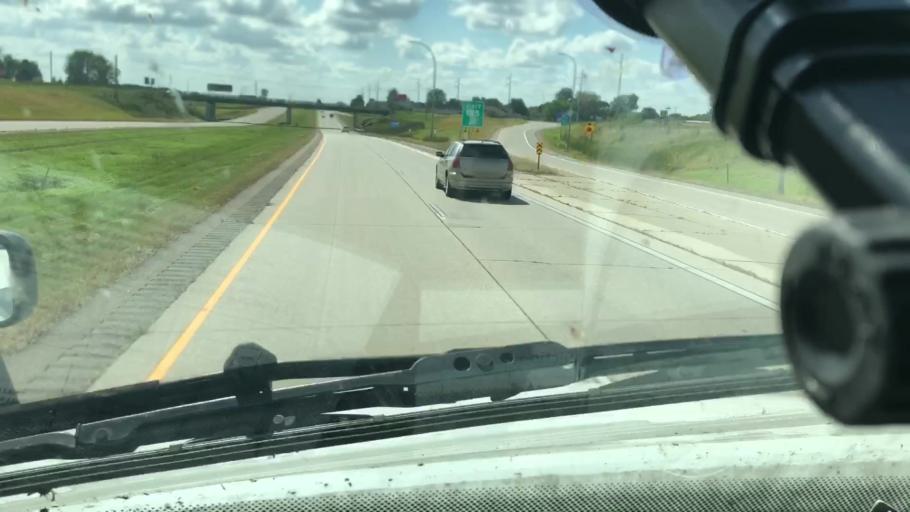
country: US
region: Minnesota
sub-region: Mower County
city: Austin
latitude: 43.6685
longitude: -93.0180
